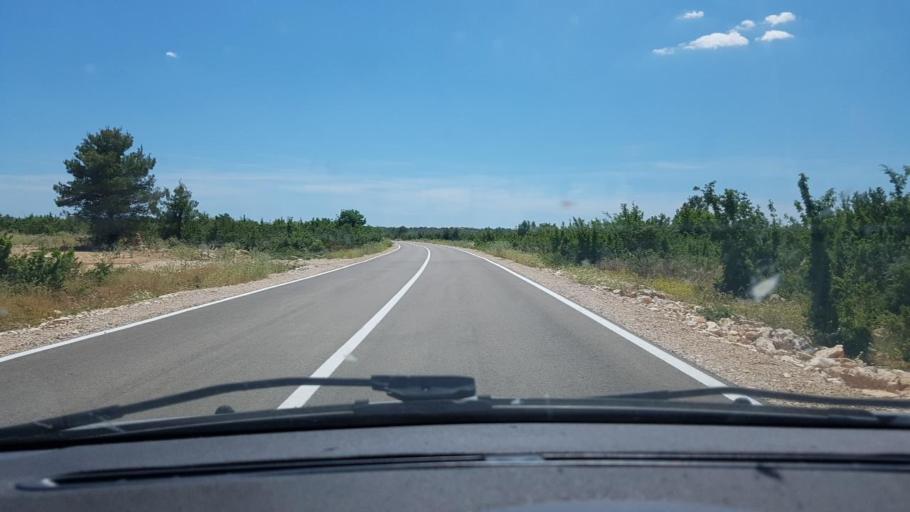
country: HR
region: Sibensko-Kniniska
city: Kistanje
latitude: 43.9370
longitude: 15.9383
